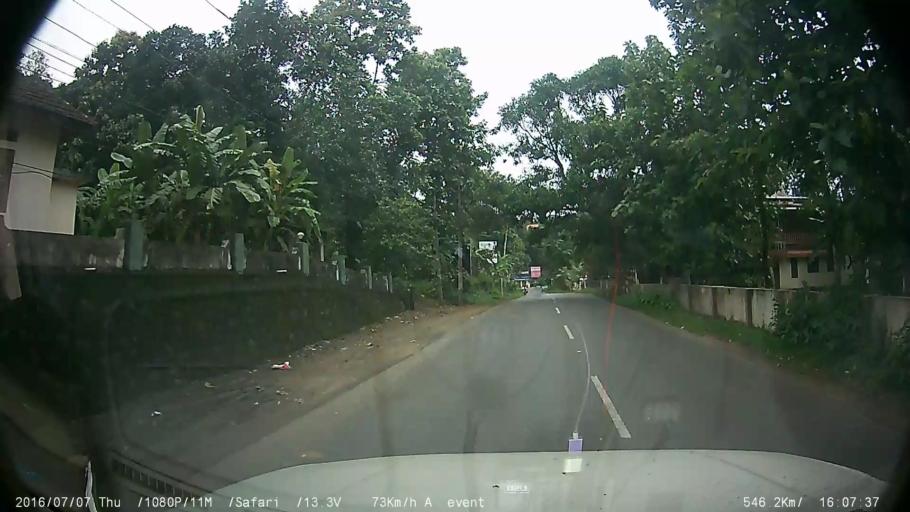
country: IN
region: Kerala
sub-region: Kottayam
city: Palackattumala
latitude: 9.8054
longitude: 76.6137
